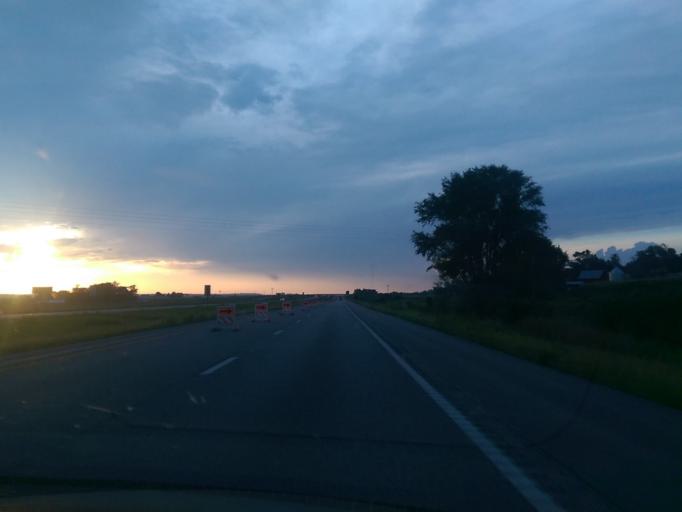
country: US
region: Missouri
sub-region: Atchison County
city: Rock Port
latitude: 40.3592
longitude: -95.5198
